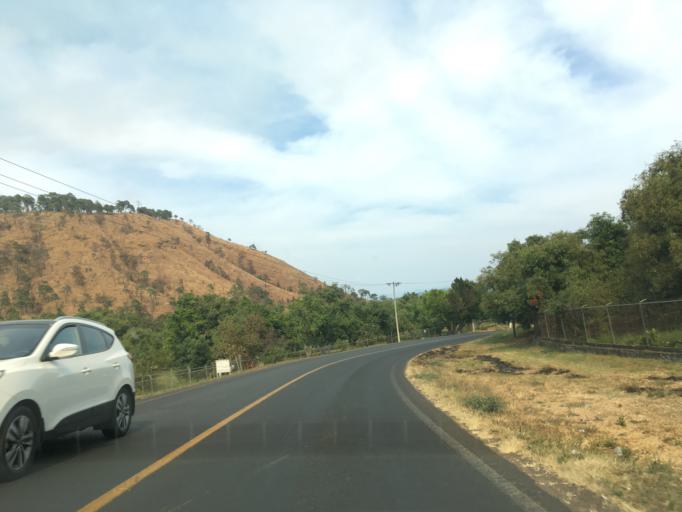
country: MX
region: Michoacan
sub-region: Uruapan
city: Uruapan
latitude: 19.3836
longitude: -102.0865
